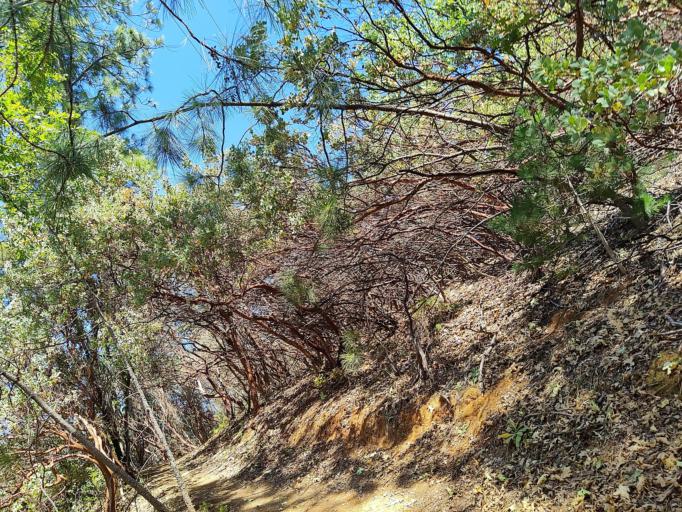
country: US
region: California
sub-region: Placer County
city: Meadow Vista
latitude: 39.0327
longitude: -120.9799
